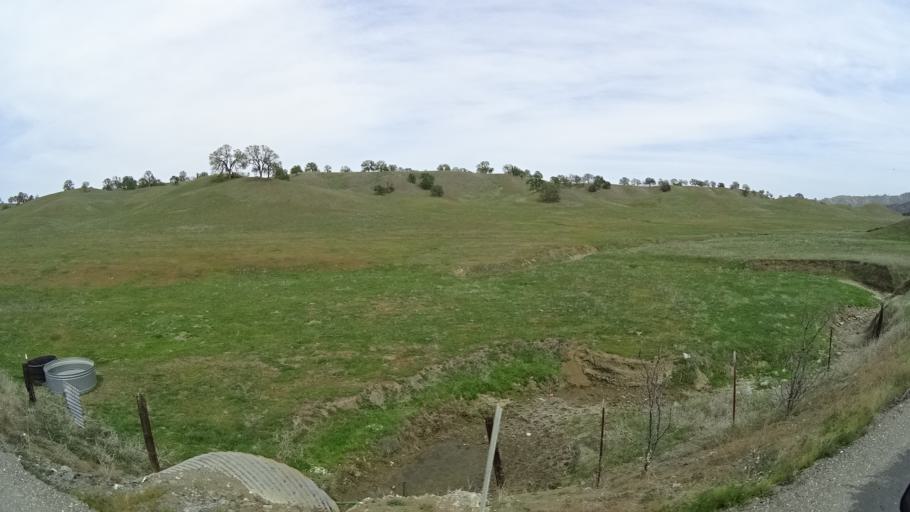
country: US
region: California
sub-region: Glenn County
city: Willows
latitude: 39.6123
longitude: -122.5675
